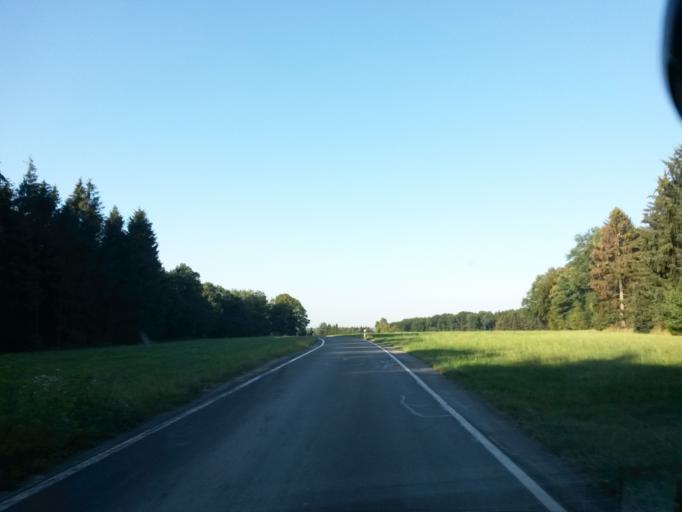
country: DE
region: North Rhine-Westphalia
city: Wipperfurth
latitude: 51.0922
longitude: 7.4107
